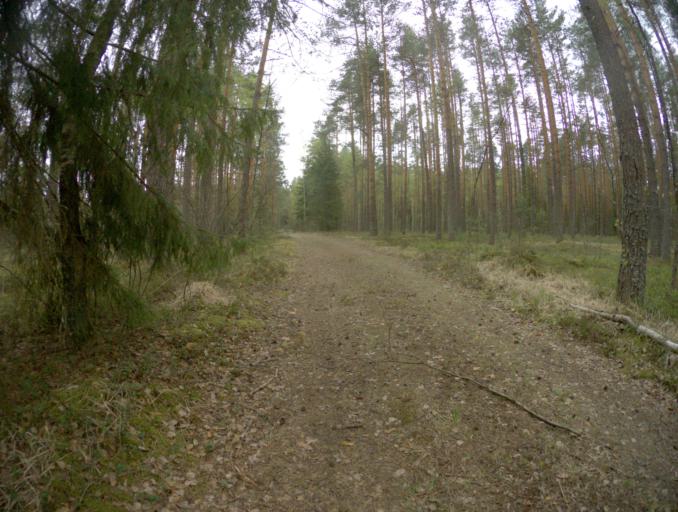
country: RU
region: Vladimir
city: Golovino
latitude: 55.9048
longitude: 40.3934
